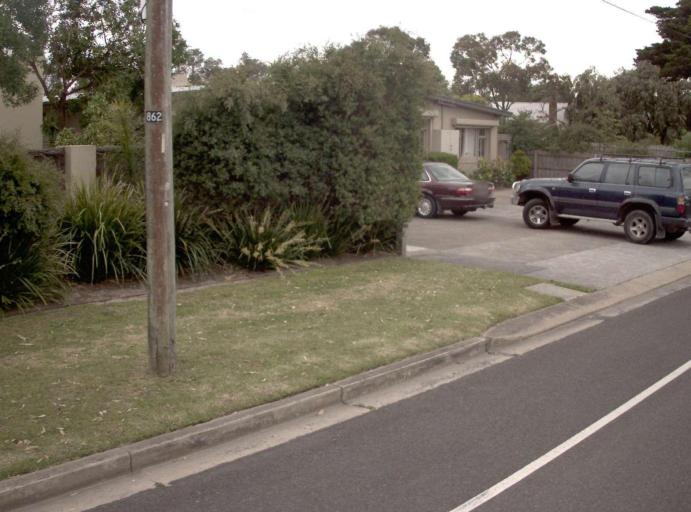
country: AU
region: Victoria
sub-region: Mornington Peninsula
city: Rosebud
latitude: -38.3540
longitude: 144.9099
